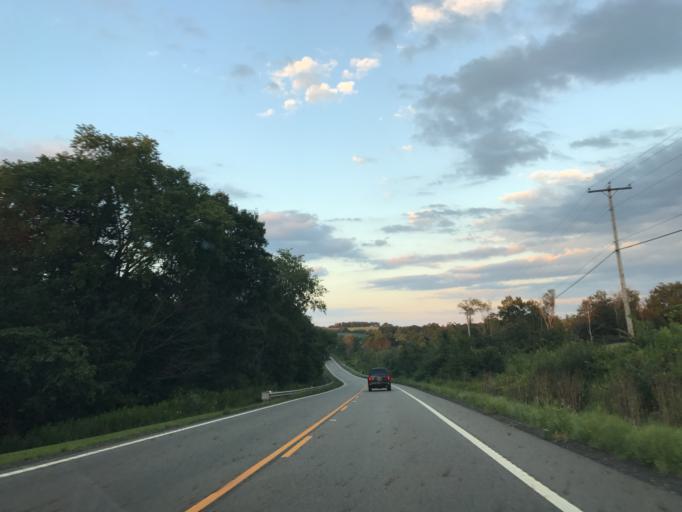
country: US
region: Ohio
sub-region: Columbiana County
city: Lisbon
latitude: 40.7658
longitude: -80.8725
